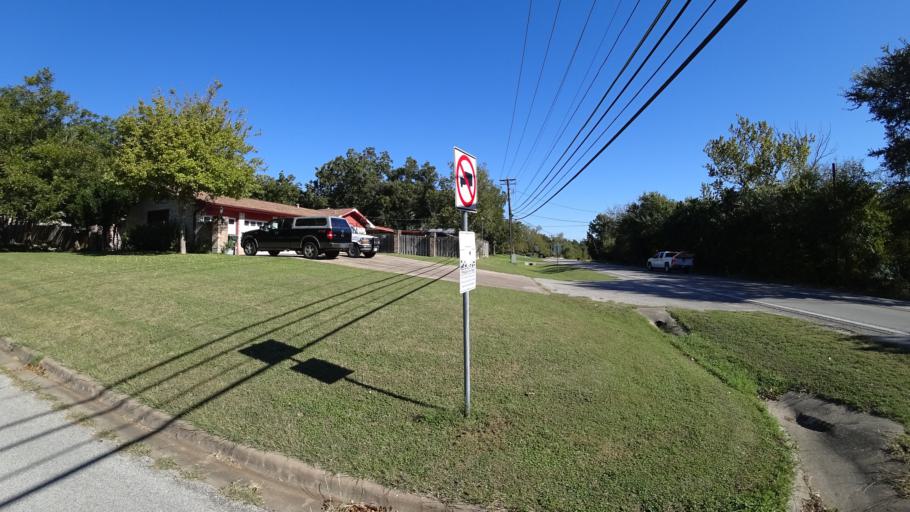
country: US
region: Texas
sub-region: Travis County
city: Manor
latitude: 30.3355
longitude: -97.6522
